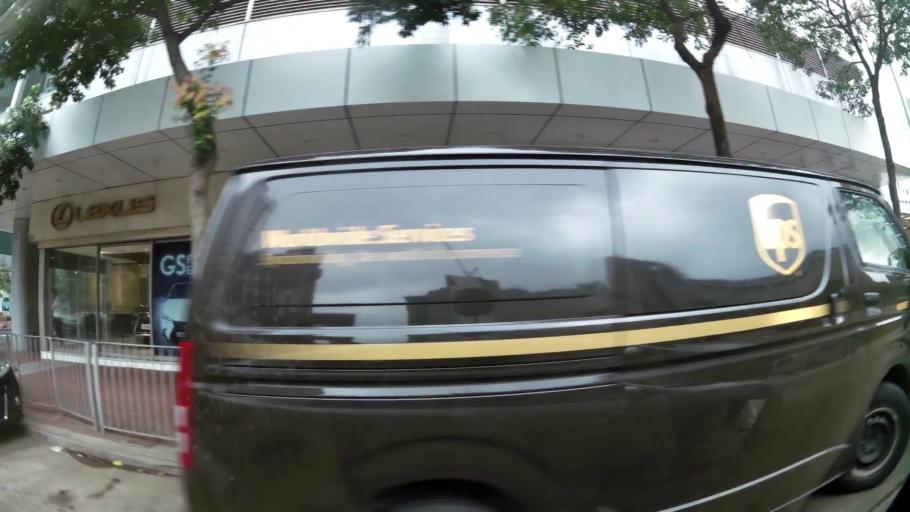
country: HK
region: Wanchai
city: Wan Chai
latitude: 22.2795
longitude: 114.1703
